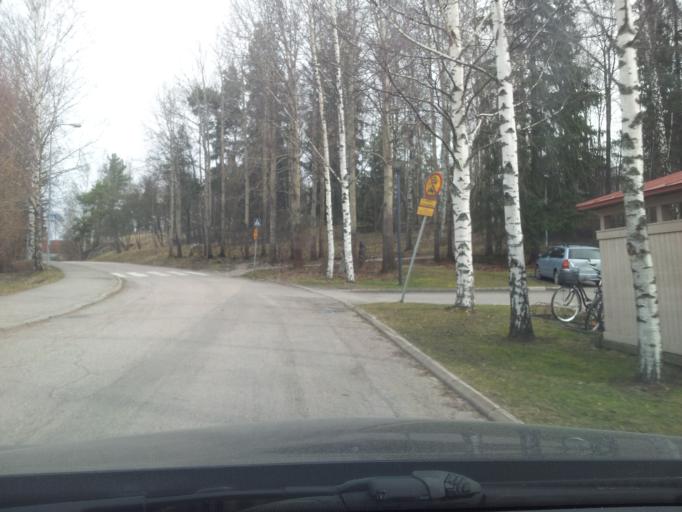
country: FI
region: Uusimaa
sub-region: Helsinki
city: Koukkuniemi
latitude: 60.1807
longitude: 24.7877
